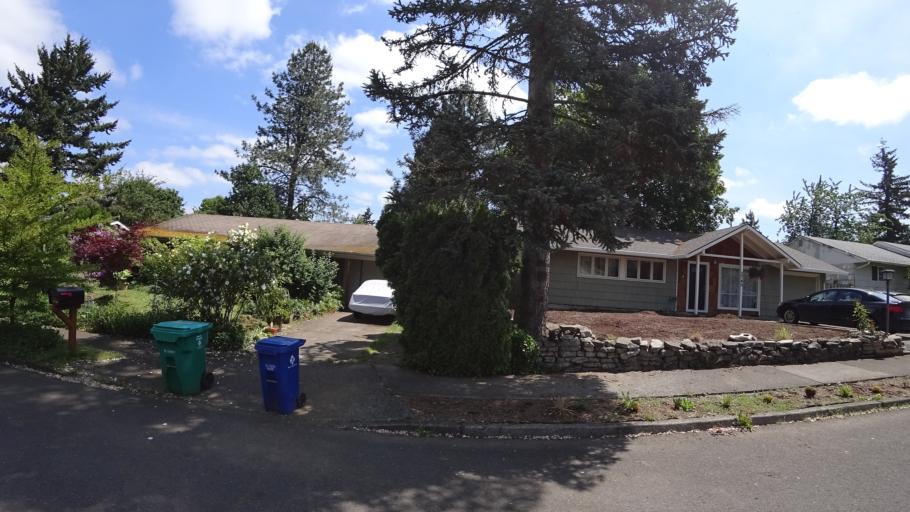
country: US
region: Oregon
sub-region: Multnomah County
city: Gresham
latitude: 45.4953
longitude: -122.4906
